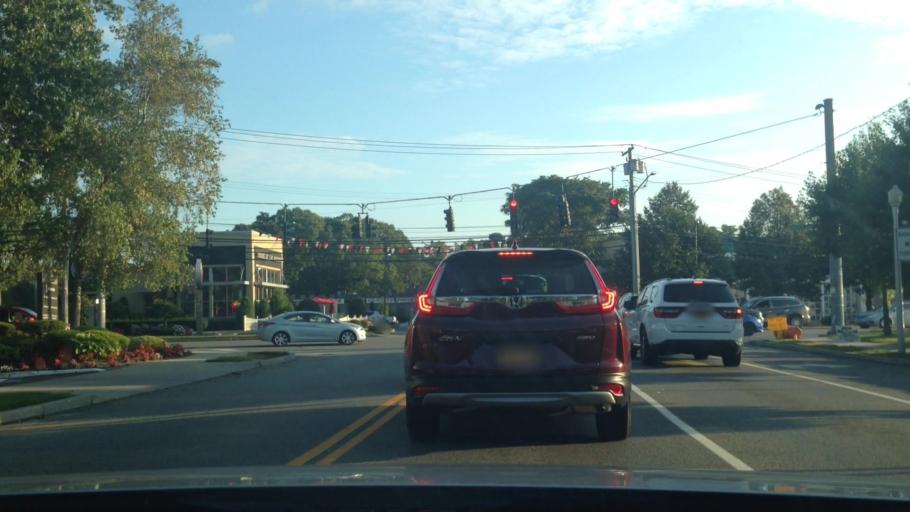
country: US
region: New York
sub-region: Suffolk County
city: Centereach
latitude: 40.8595
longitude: -73.0792
